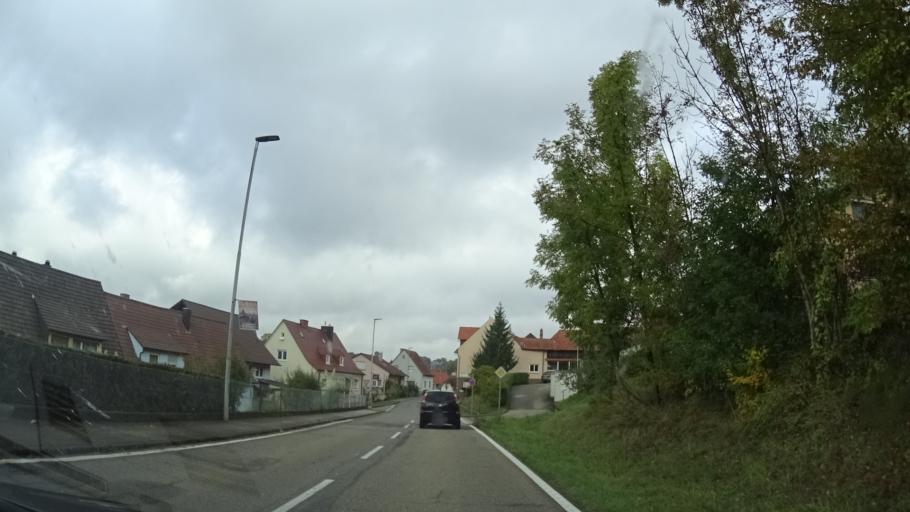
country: DE
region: Baden-Wuerttemberg
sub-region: Karlsruhe Region
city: Eisingen
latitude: 48.9606
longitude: 8.6443
